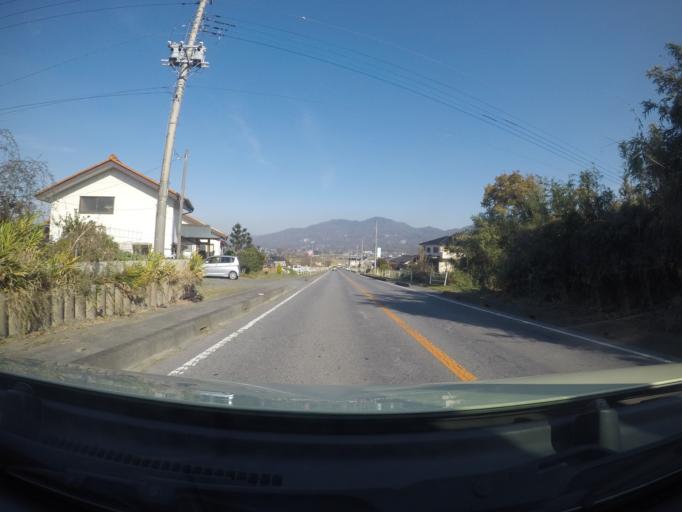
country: JP
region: Ibaraki
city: Makabe
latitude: 36.2662
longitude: 140.0942
